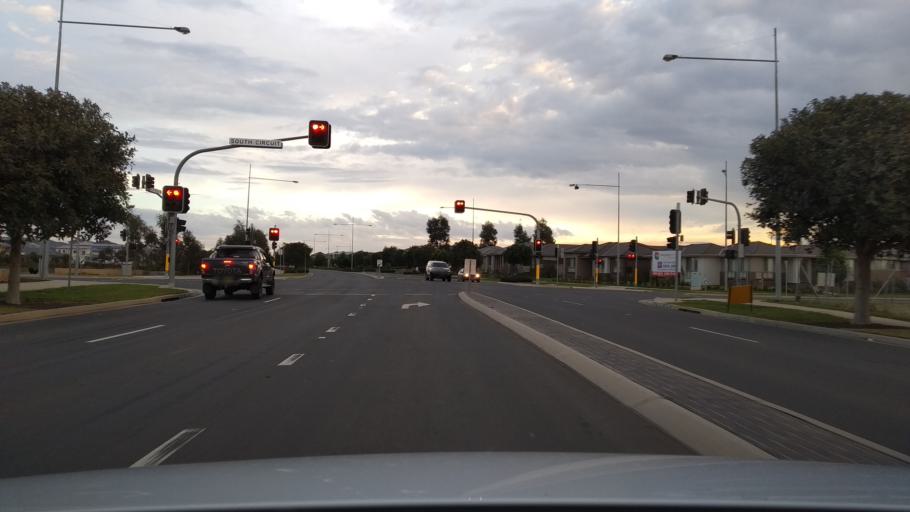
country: AU
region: New South Wales
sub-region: Camden
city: Narellan
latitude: -34.0015
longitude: 150.7356
